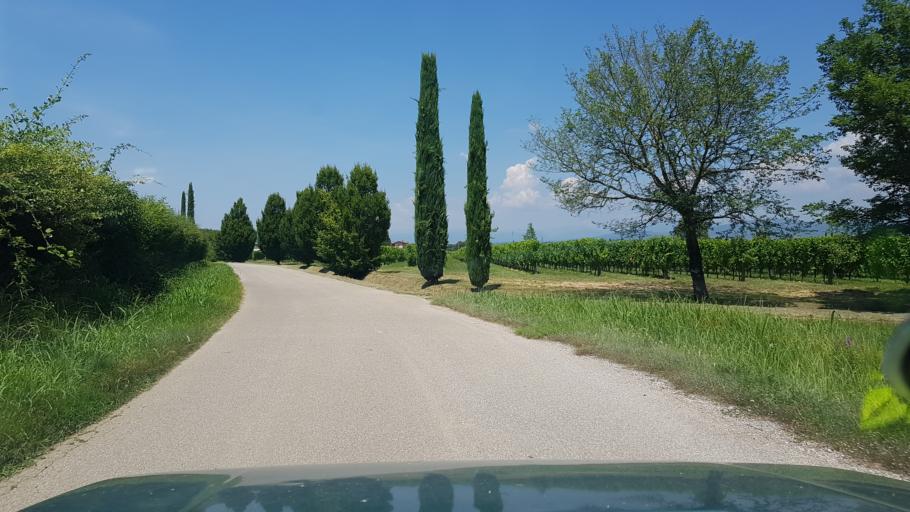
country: IT
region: Friuli Venezia Giulia
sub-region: Provincia di Gorizia
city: Farra d'Isonzo
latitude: 45.9096
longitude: 13.5388
